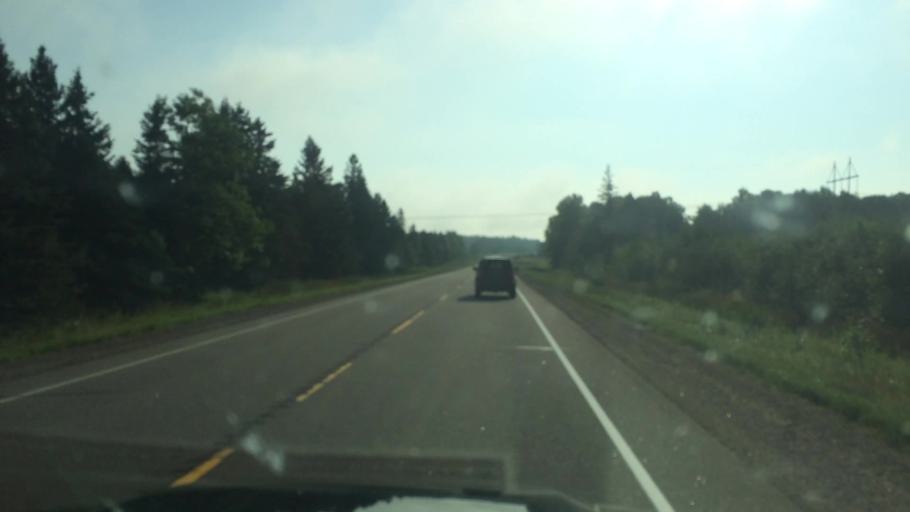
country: US
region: Wisconsin
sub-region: Langlade County
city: Antigo
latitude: 45.1452
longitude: -89.2894
